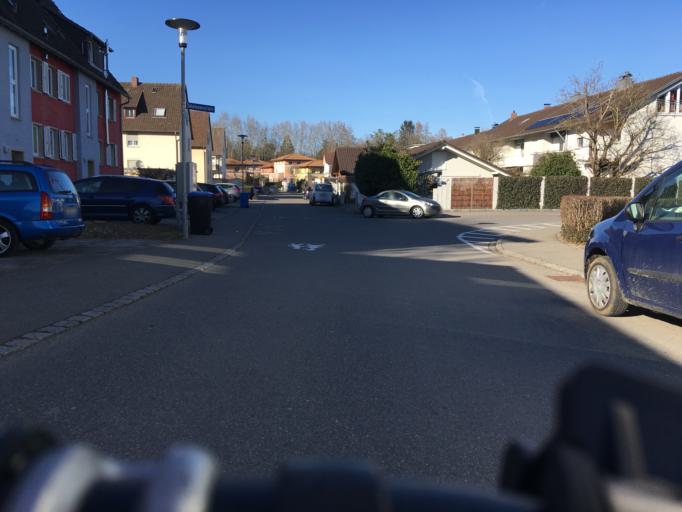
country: DE
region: Baden-Wuerttemberg
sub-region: Freiburg Region
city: Rielasingen-Worblingen
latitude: 47.7260
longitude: 8.8424
